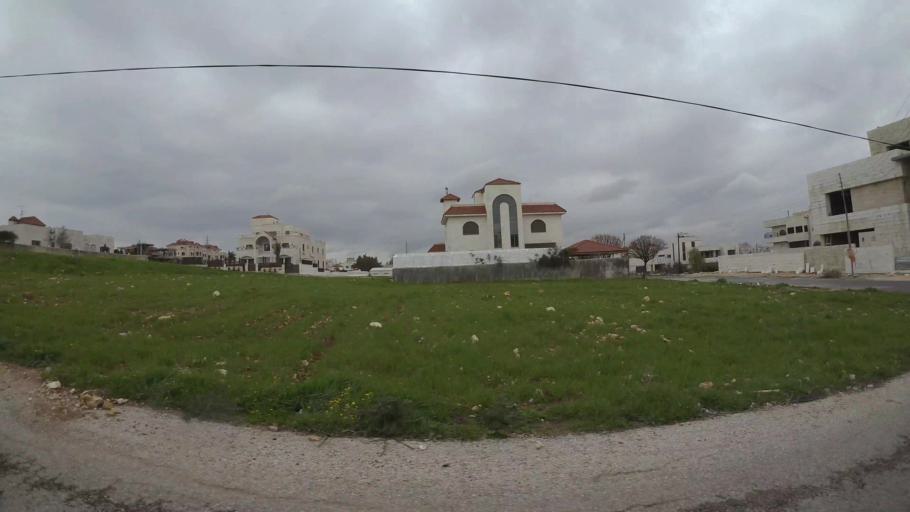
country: JO
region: Amman
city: Umm as Summaq
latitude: 31.9252
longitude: 35.8572
